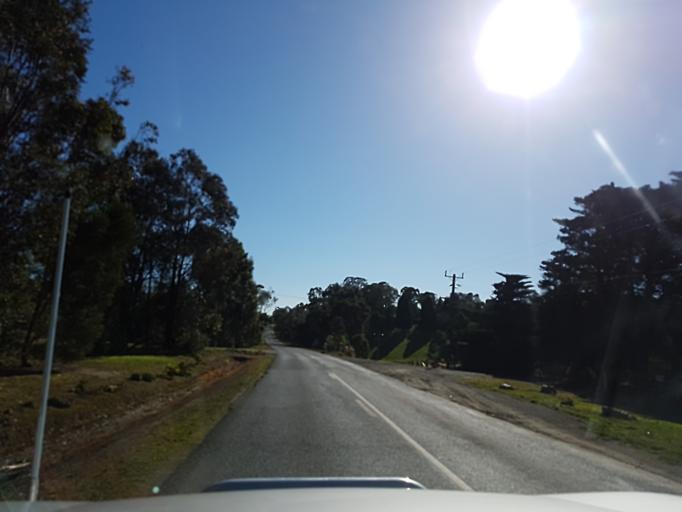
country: AU
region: Victoria
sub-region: Yarra Ranges
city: Yarra Glen
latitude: -37.6394
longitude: 145.3745
